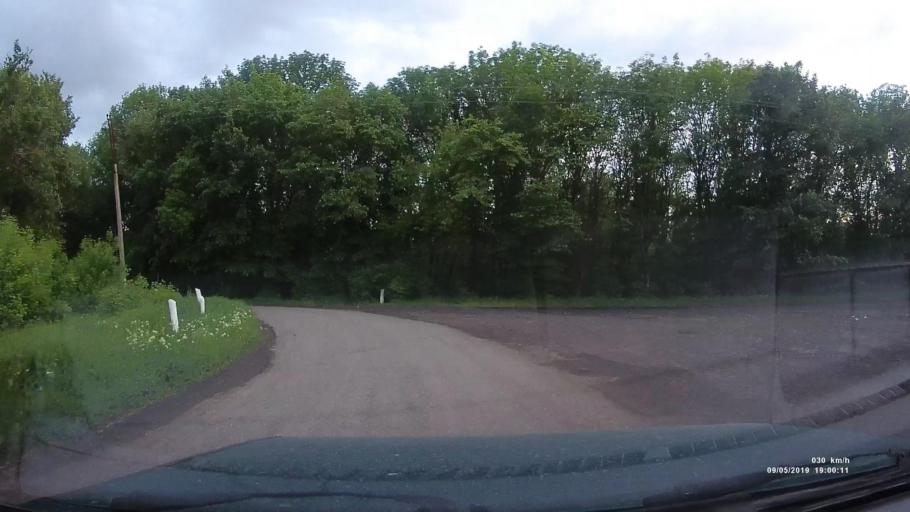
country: RU
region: Krasnodarskiy
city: Kanelovskaya
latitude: 46.7526
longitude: 39.1350
